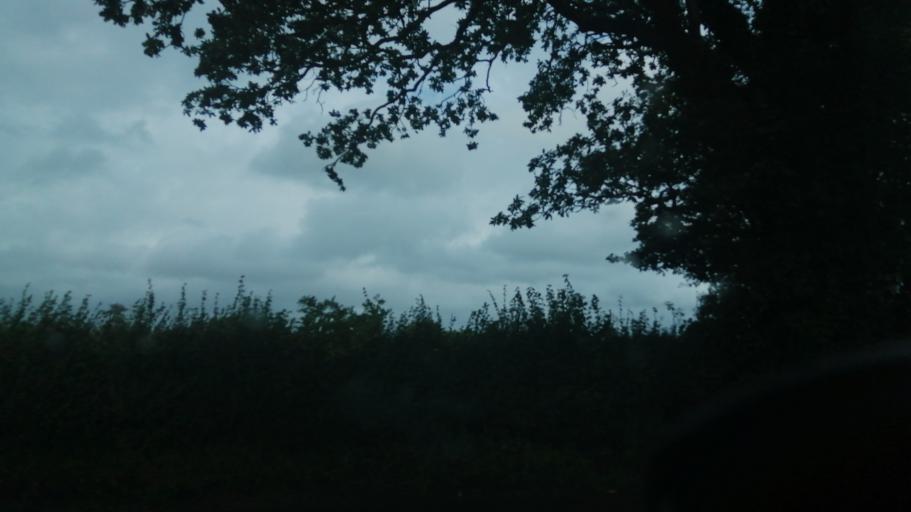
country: GB
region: England
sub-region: Herefordshire
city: Kingstone
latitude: 52.0194
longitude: -2.8529
